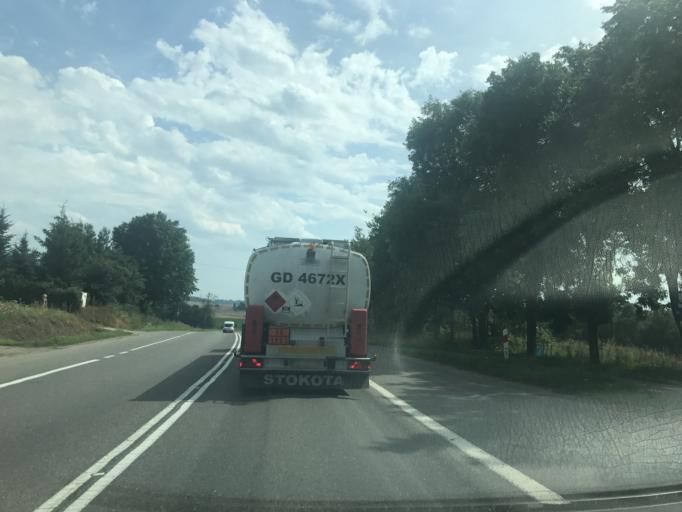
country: PL
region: Warmian-Masurian Voivodeship
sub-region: Powiat ostrodzki
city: Ostroda
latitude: 53.6609
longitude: 20.0468
